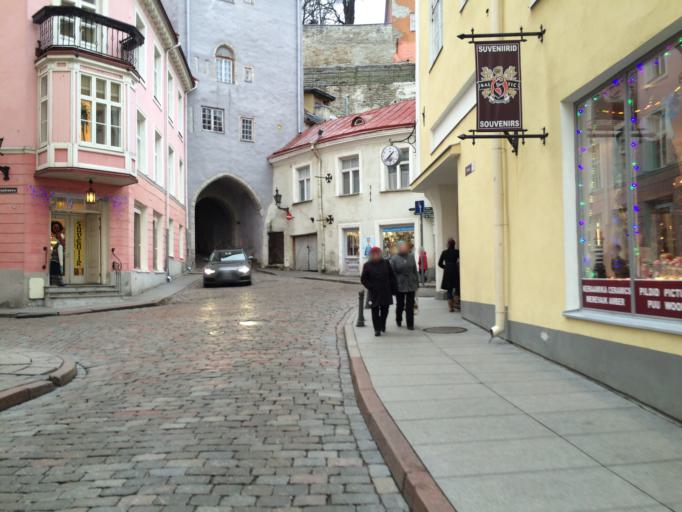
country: EE
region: Harju
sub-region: Tallinna linn
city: Tallinn
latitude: 59.4378
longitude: 24.7434
